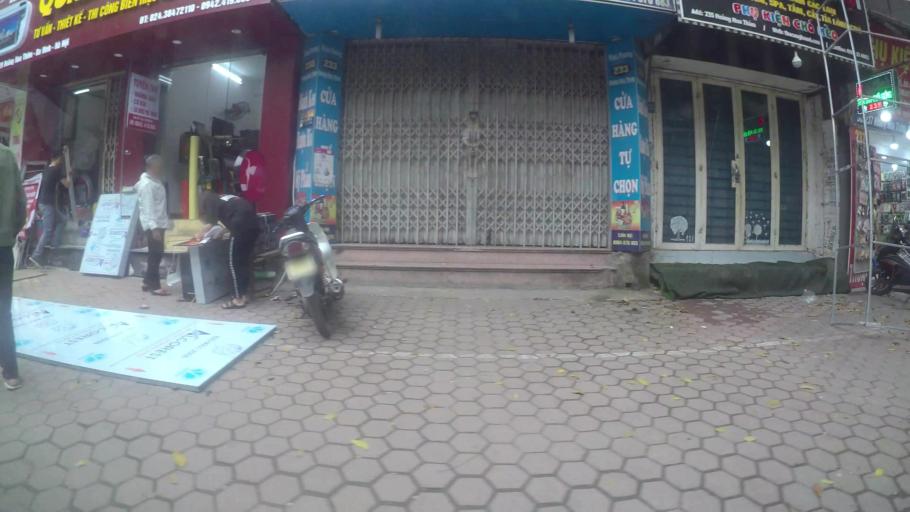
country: VN
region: Ha Noi
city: Cau Giay
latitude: 21.0420
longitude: 105.8198
